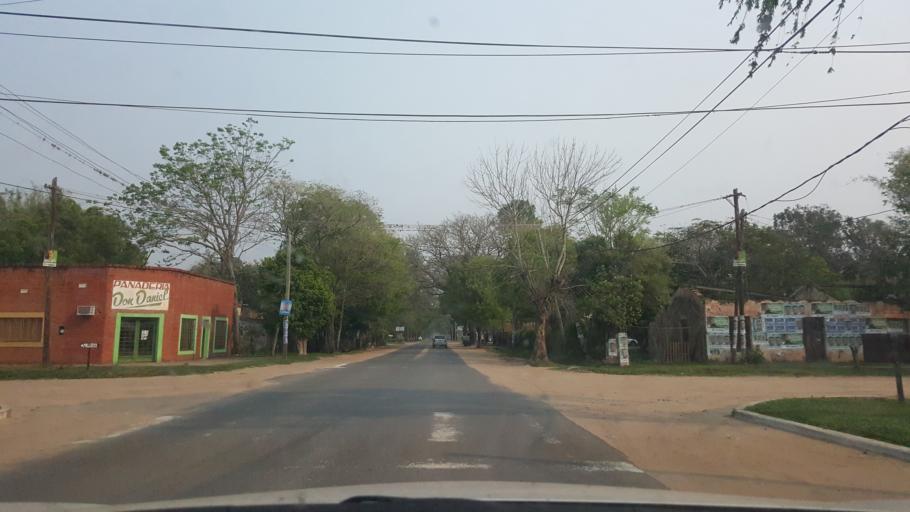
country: AR
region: Corrientes
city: Ita Ibate
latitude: -27.4290
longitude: -57.3382
